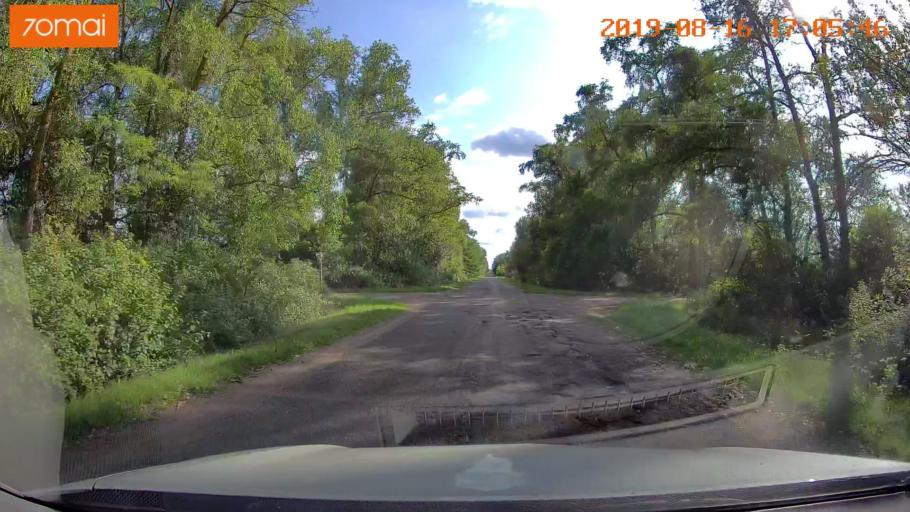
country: BY
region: Mogilev
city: Hlusha
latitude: 53.2341
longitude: 28.9406
